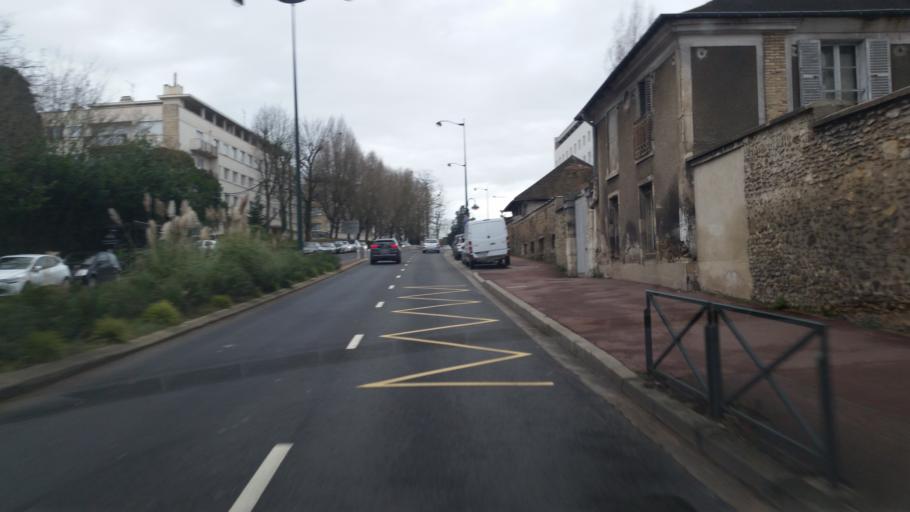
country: FR
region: Ile-de-France
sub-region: Departement des Hauts-de-Seine
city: Marnes-la-Coquette
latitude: 48.8380
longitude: 2.1686
